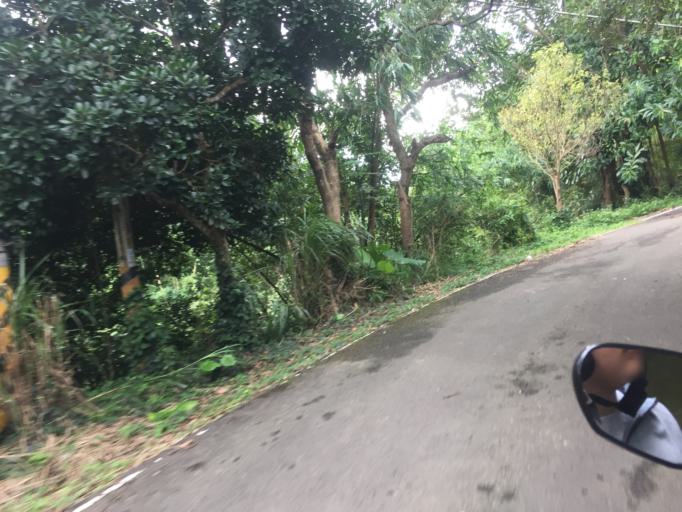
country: TW
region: Taiwan
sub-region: Hsinchu
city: Zhubei
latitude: 24.7868
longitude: 121.1602
